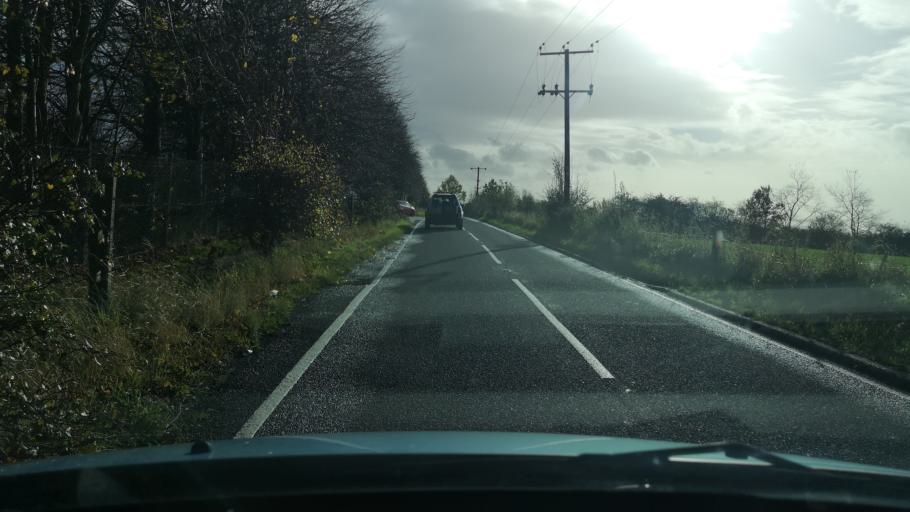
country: GB
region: England
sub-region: City and Borough of Wakefield
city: Crofton
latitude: 53.6474
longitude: -1.4193
